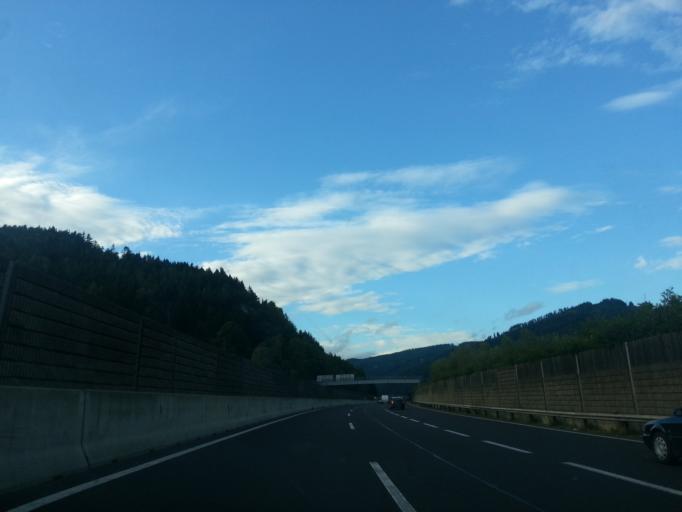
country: AT
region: Styria
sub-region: Politischer Bezirk Leoben
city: Sankt Michael in Obersteiermark
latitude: 47.3409
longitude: 15.0072
